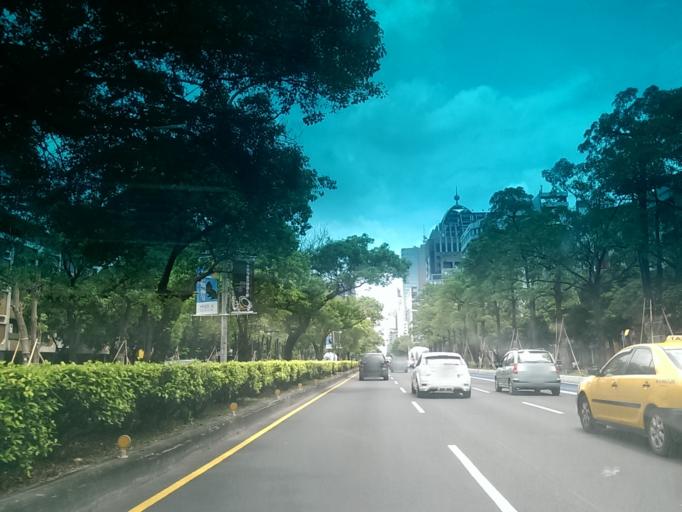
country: TW
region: Taiwan
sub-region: Taichung City
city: Taichung
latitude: 24.1603
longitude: 120.6539
